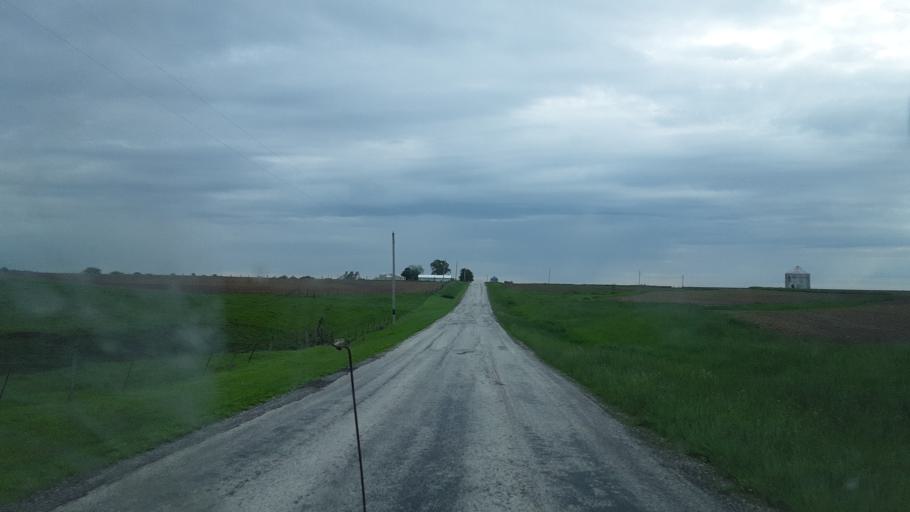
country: US
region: Illinois
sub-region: McDonough County
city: Macomb
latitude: 40.3819
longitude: -90.5906
